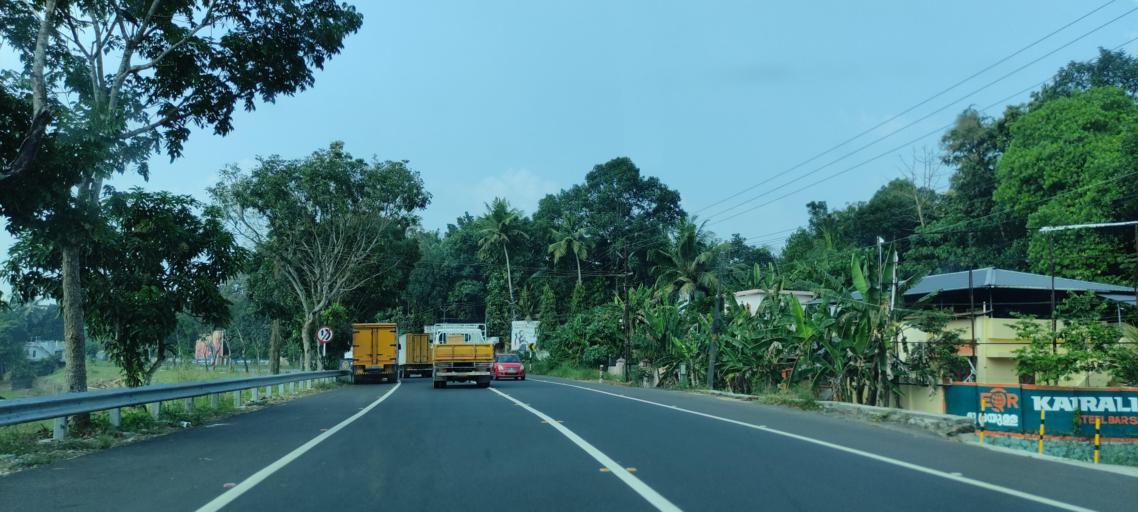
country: IN
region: Kerala
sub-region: Alappuzha
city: Chengannur
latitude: 9.2574
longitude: 76.6598
